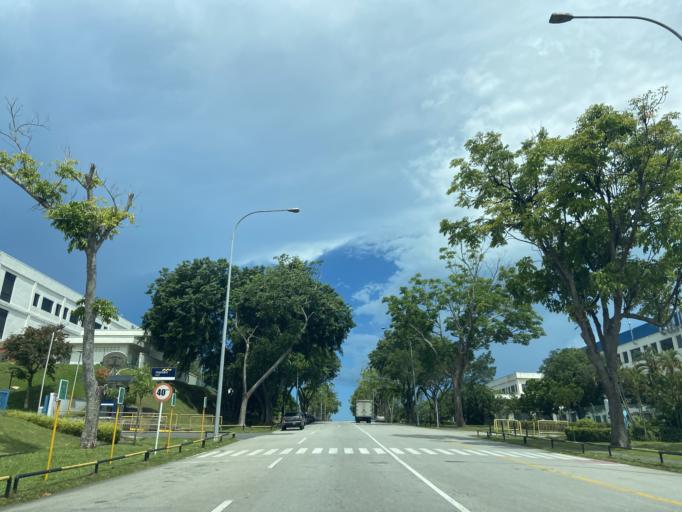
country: SG
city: Singapore
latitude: 1.0665
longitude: 104.0286
